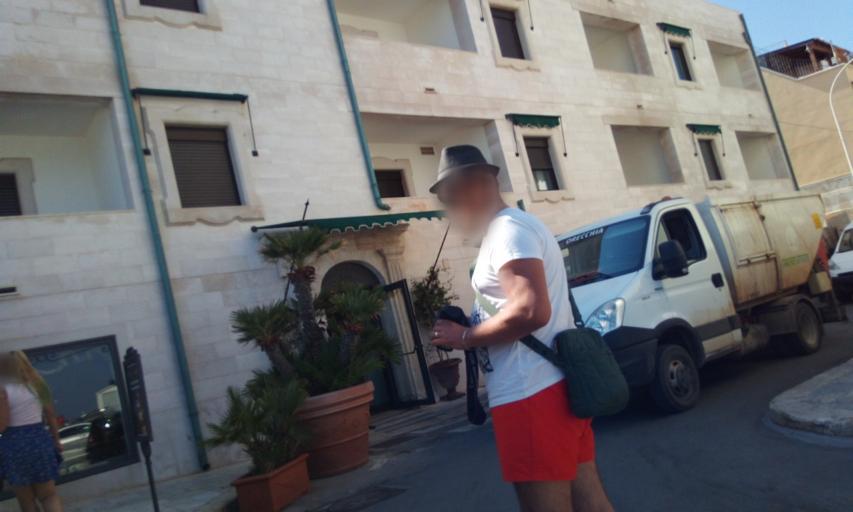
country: IT
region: Apulia
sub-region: Provincia di Bari
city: Polignano a Mare
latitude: 40.9969
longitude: 17.2176
